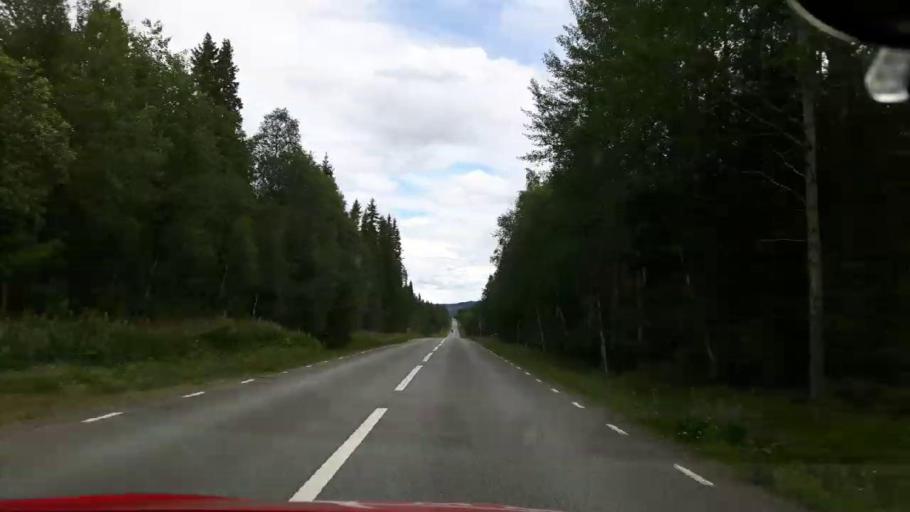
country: NO
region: Nord-Trondelag
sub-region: Lierne
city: Sandvika
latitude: 64.3898
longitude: 14.4242
